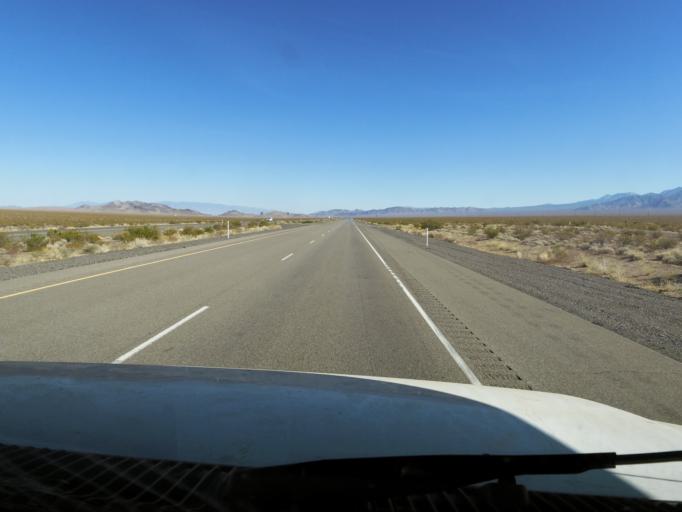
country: US
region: Nevada
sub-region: Nye County
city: Pahrump
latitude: 36.5936
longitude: -115.9421
